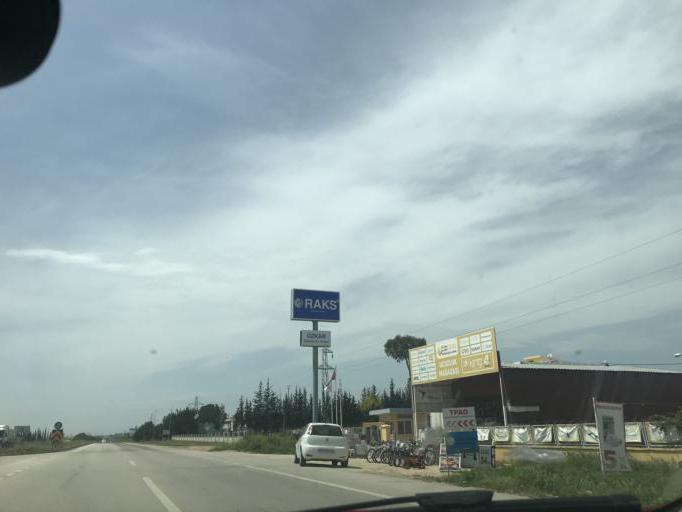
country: TR
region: Adana
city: Yuregir
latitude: 36.9754
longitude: 35.4896
